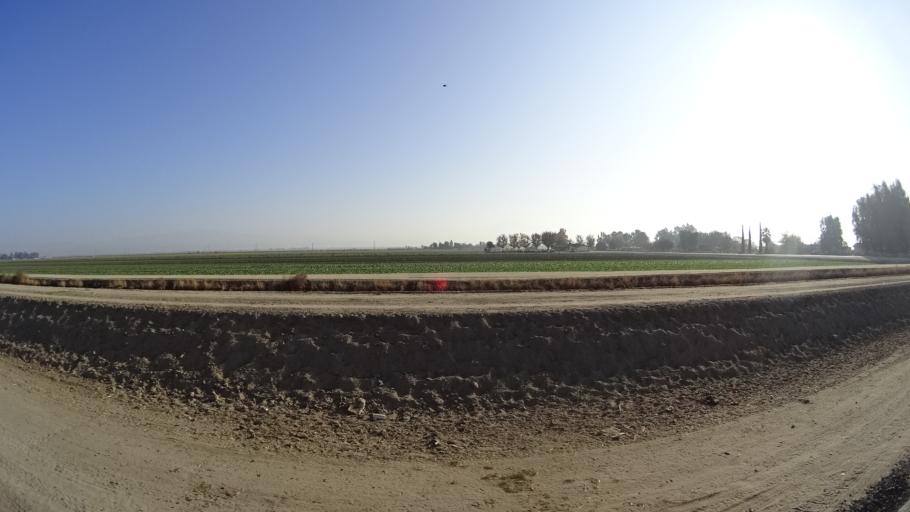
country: US
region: California
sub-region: Kern County
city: Greenfield
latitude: 35.2535
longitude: -118.9854
